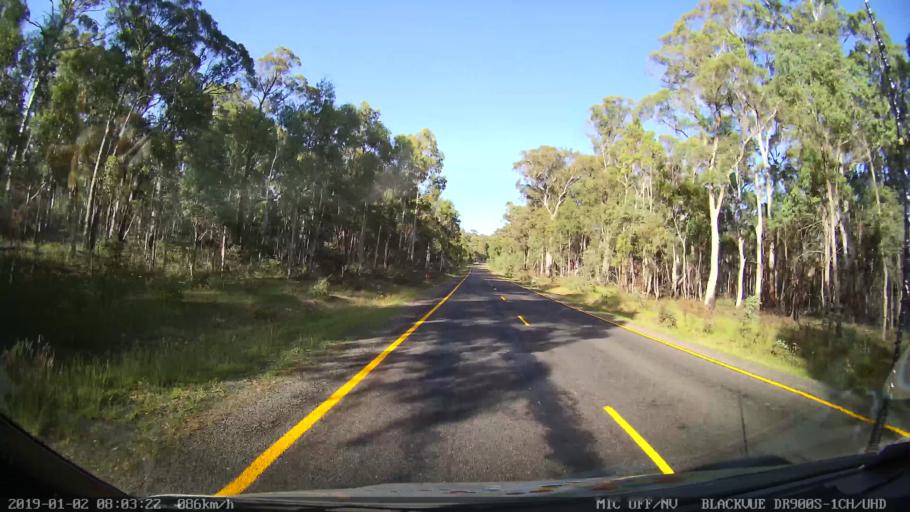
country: AU
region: New South Wales
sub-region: Tumut Shire
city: Tumut
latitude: -35.6622
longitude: 148.4096
